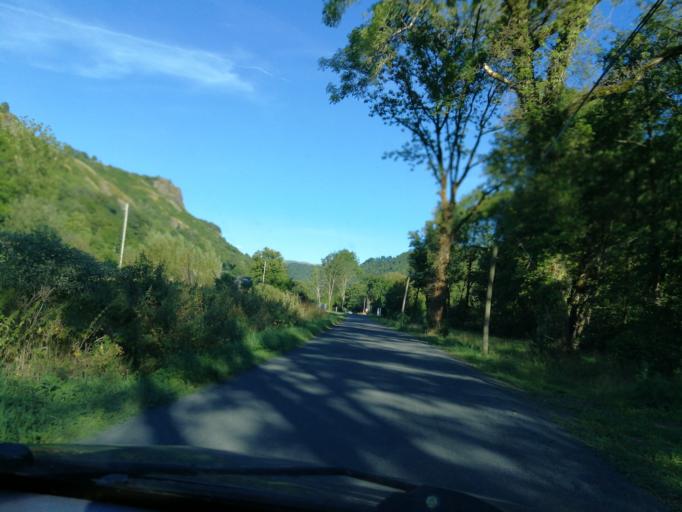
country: FR
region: Auvergne
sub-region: Departement du Cantal
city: Saint-Cernin
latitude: 45.1040
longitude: 2.5254
